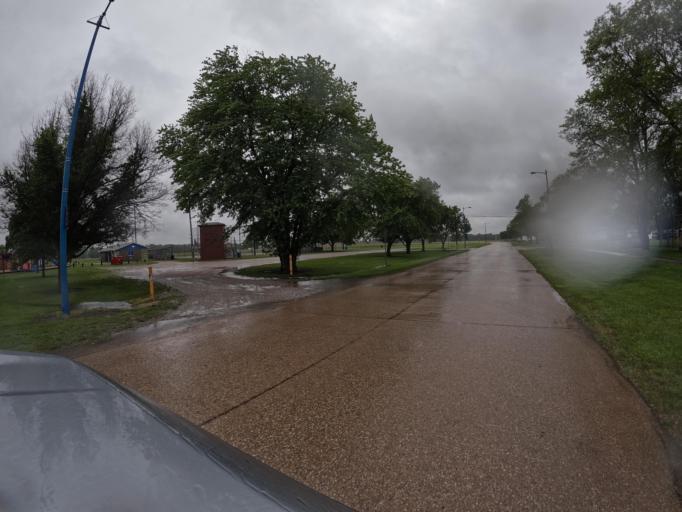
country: US
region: Nebraska
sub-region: Saline County
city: Wilber
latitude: 40.3945
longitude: -96.9258
